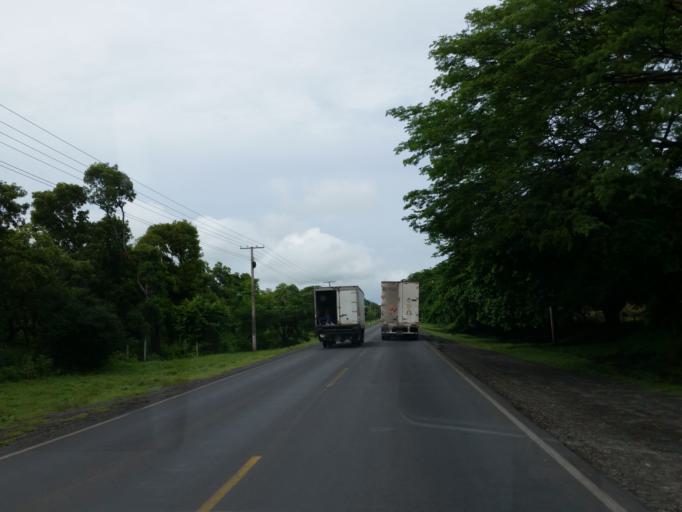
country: NI
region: Leon
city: Nagarote
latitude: 12.2733
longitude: -86.5339
